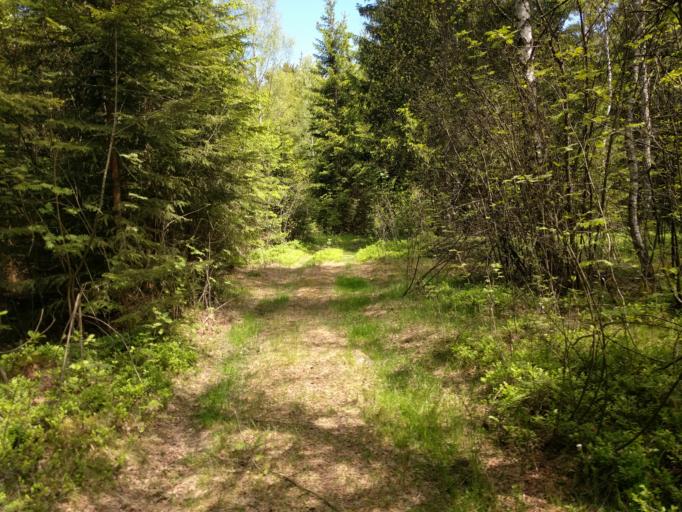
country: AT
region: Lower Austria
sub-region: Politischer Bezirk Zwettl
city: Langschlag
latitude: 48.5850
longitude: 14.8987
